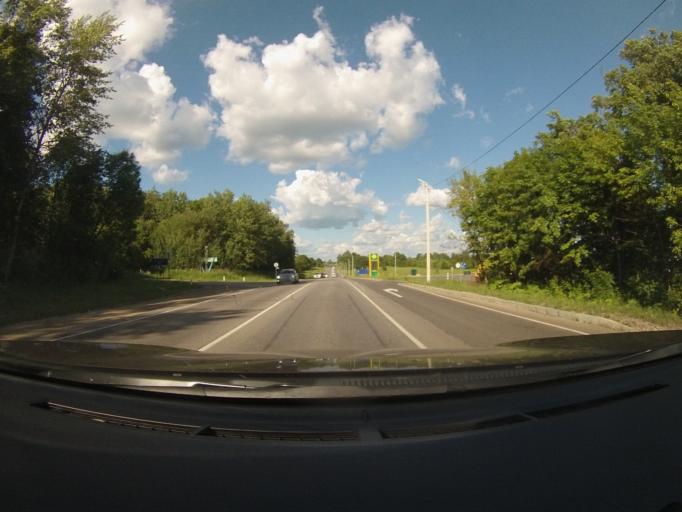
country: RU
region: Tula
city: Bol'shoye Skuratovo
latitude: 53.4509
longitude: 36.8555
